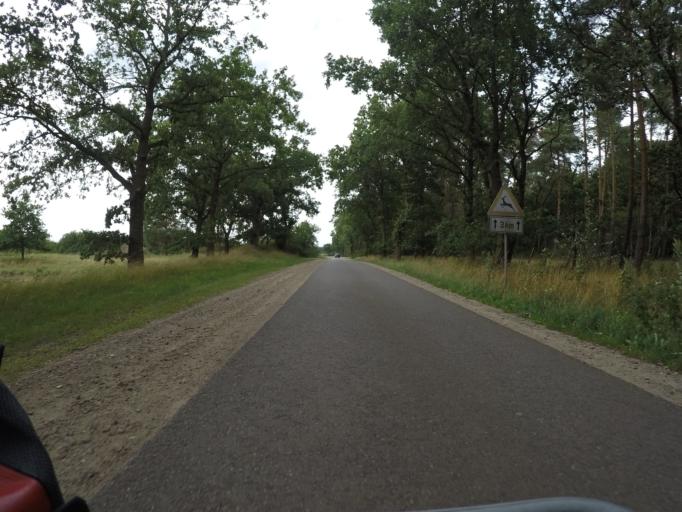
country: DE
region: Lower Saxony
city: Bardowick
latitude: 53.3067
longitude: 10.4033
